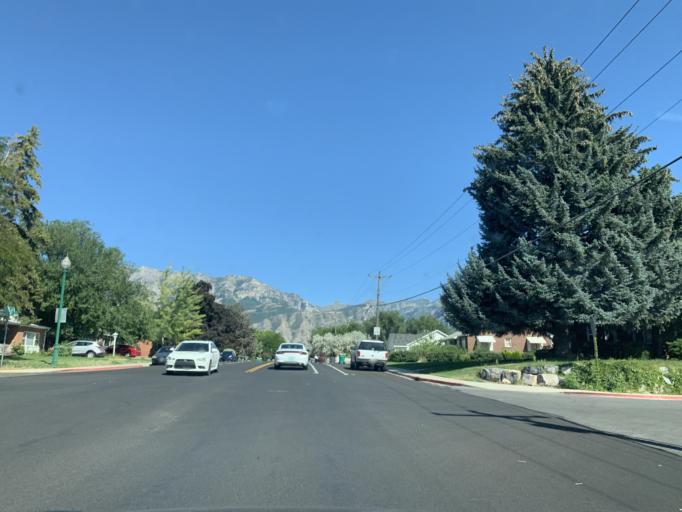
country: US
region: Utah
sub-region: Utah County
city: Orem
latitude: 40.2826
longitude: -111.7099
